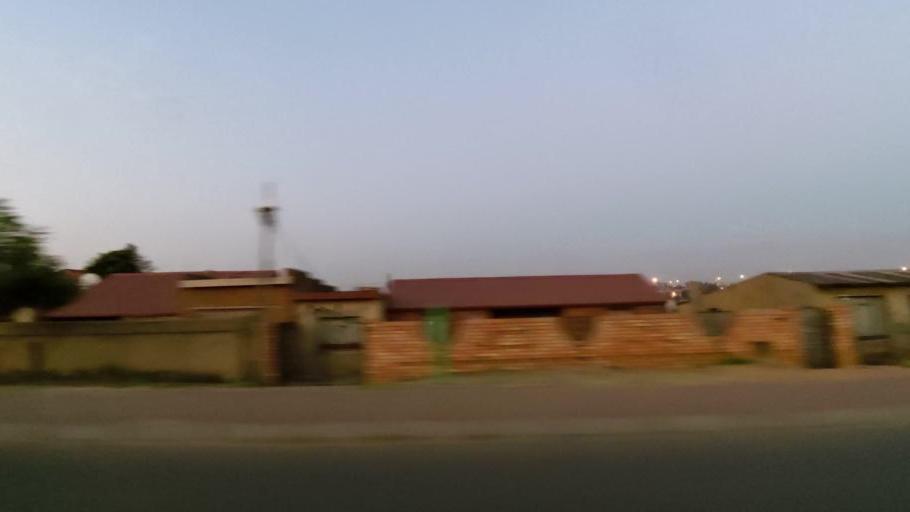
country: ZA
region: Gauteng
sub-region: City of Johannesburg Metropolitan Municipality
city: Soweto
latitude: -26.2337
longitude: 27.9123
